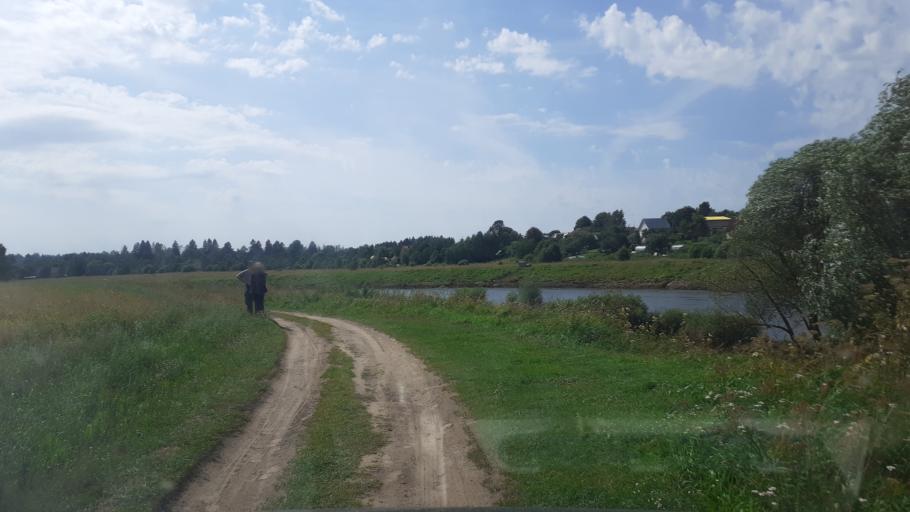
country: RU
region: Moskovskaya
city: Kolyubakino
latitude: 55.6445
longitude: 36.5774
